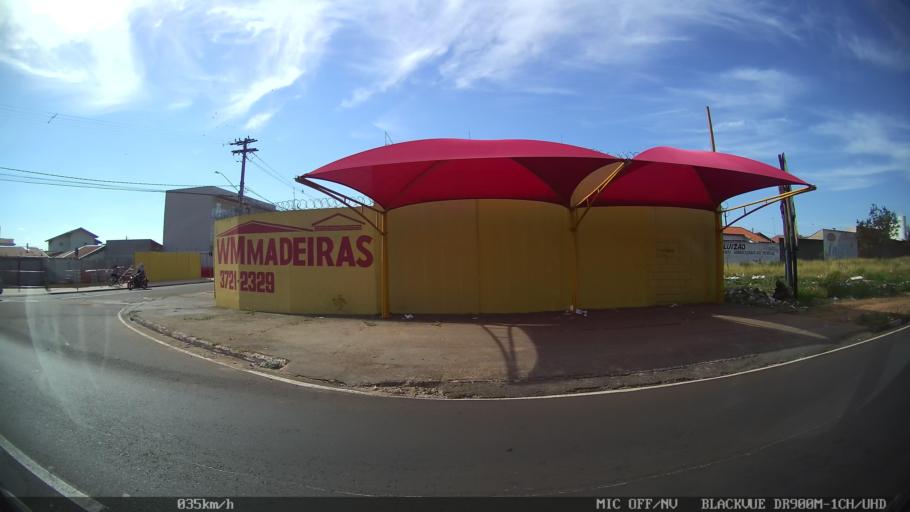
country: BR
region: Sao Paulo
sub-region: Franca
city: Franca
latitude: -20.5273
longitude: -47.4305
